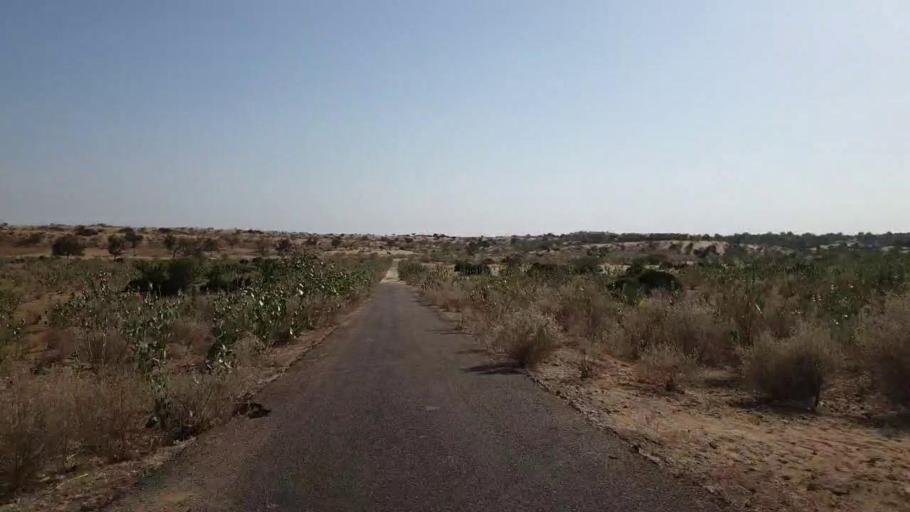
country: PK
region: Sindh
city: Nabisar
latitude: 25.0522
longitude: 70.0220
